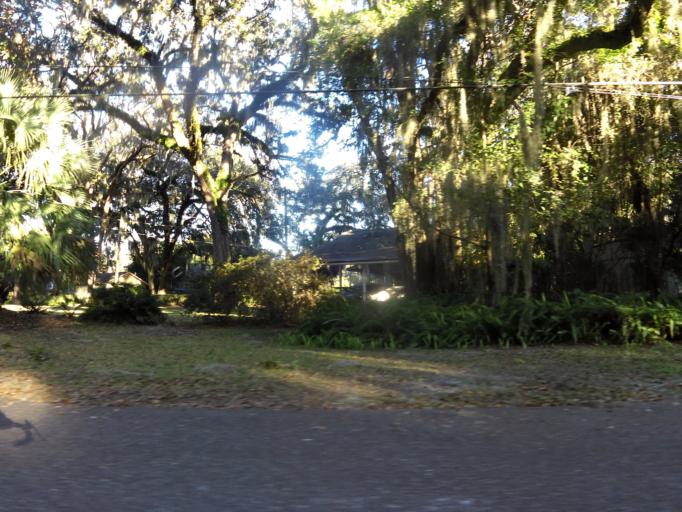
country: US
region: Florida
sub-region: Duval County
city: Jacksonville
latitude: 30.2771
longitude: -81.7023
